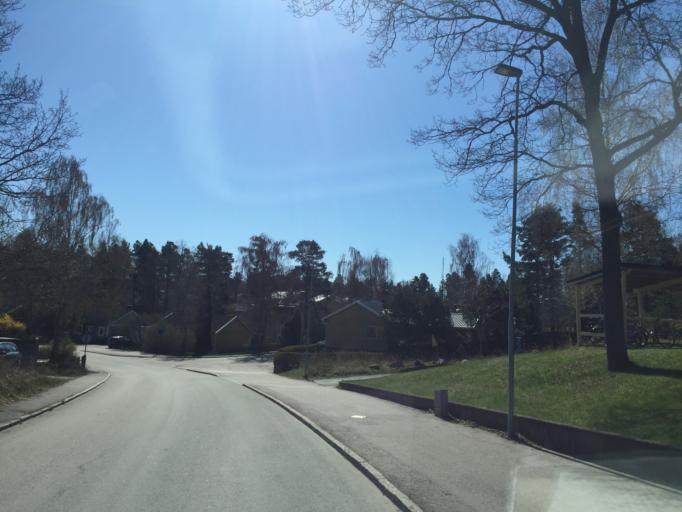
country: SE
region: Kalmar
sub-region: Oskarshamns Kommun
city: Oskarshamn
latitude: 57.2560
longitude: 16.4509
